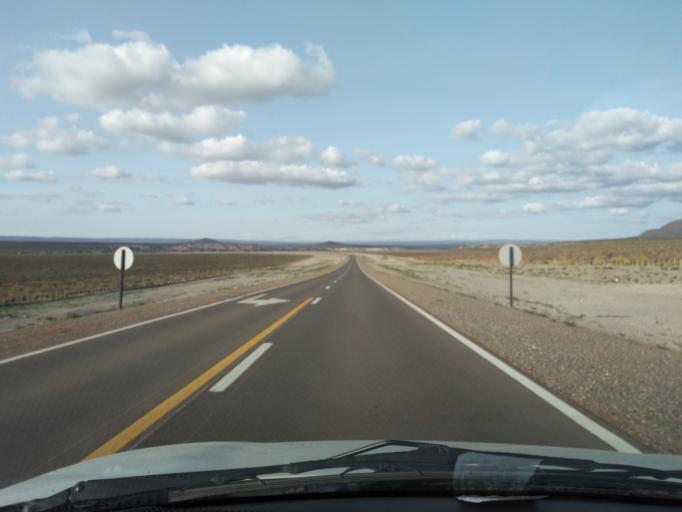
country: AR
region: Mendoza
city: San Rafael
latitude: -34.6566
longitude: -69.1600
